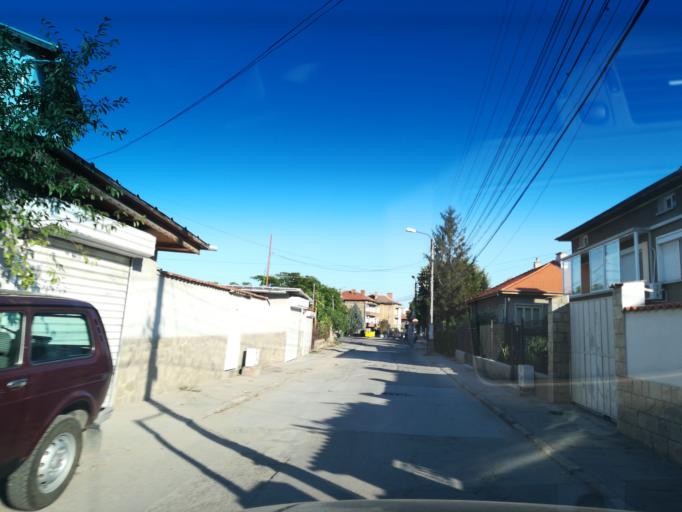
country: BG
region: Stara Zagora
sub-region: Obshtina Chirpan
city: Chirpan
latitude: 42.1046
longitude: 25.2196
